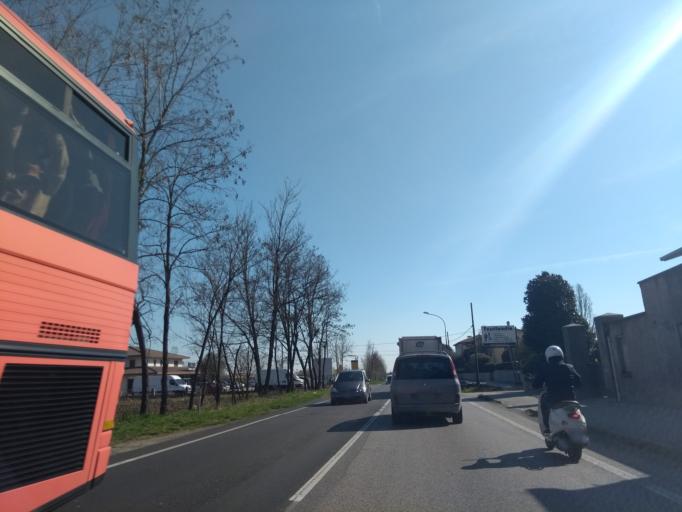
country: IT
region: Veneto
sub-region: Provincia di Vicenza
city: Belvedere
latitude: 45.6775
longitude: 11.7749
